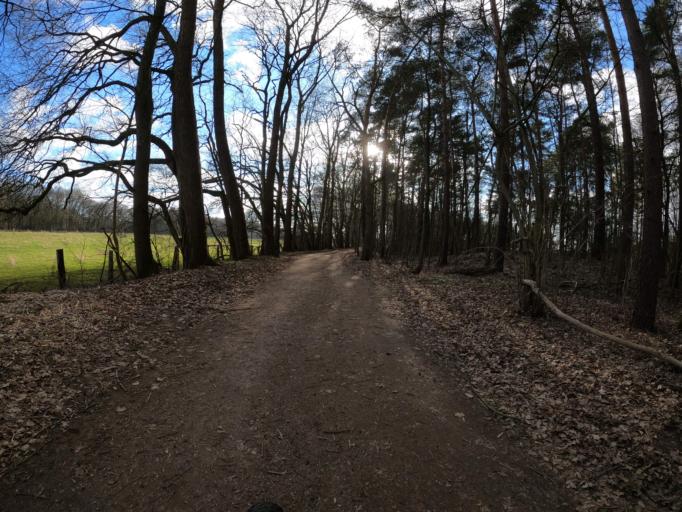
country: DE
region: Lower Saxony
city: Haselunne
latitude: 52.6609
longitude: 7.4705
